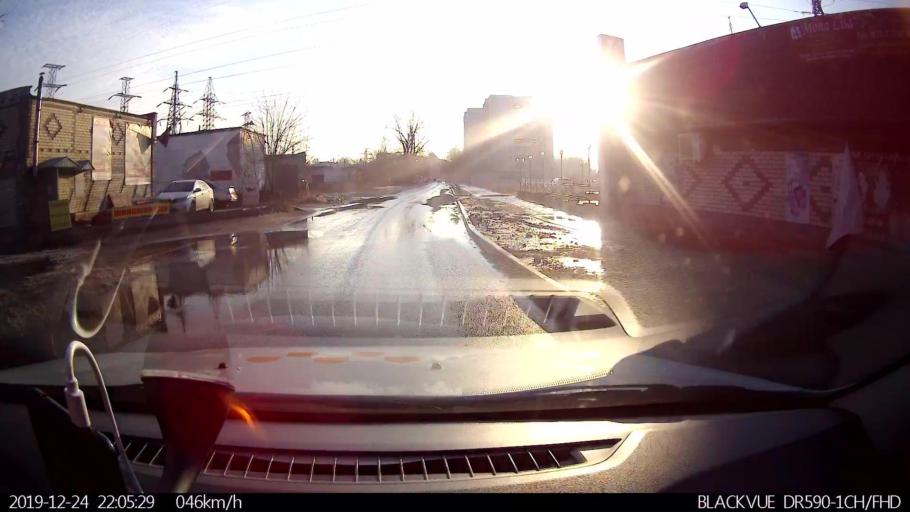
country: RU
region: Nizjnij Novgorod
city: Nizhniy Novgorod
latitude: 56.3204
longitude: 43.8809
